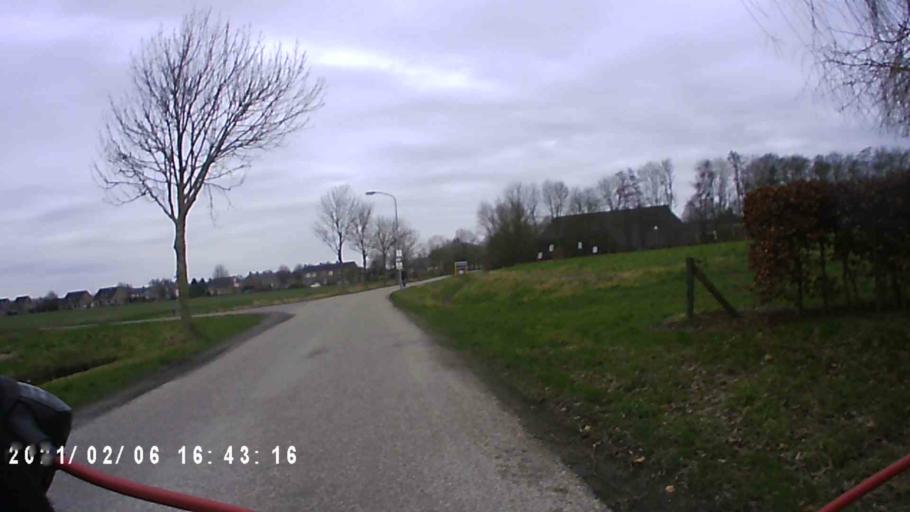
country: NL
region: Groningen
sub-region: Gemeente Bedum
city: Bedum
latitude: 53.4171
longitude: 6.7197
